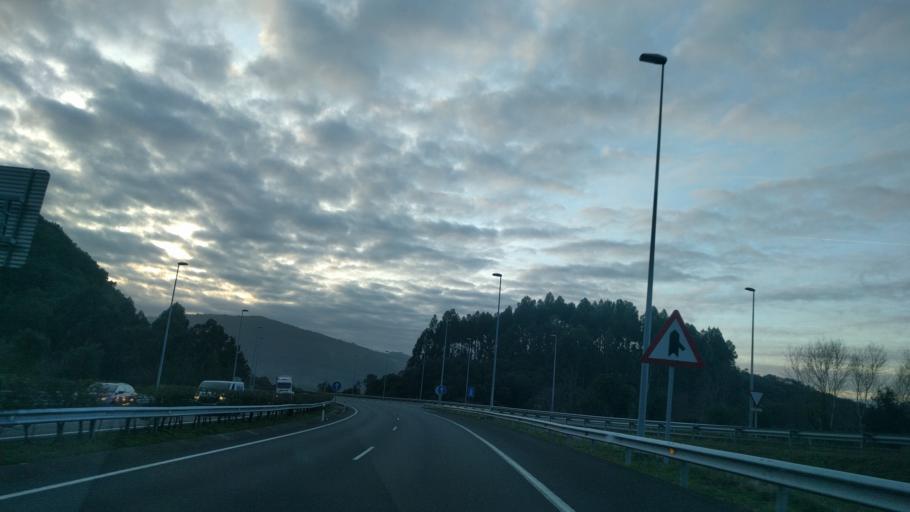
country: ES
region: Cantabria
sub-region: Provincia de Cantabria
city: Liendo
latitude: 43.3912
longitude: -3.3558
